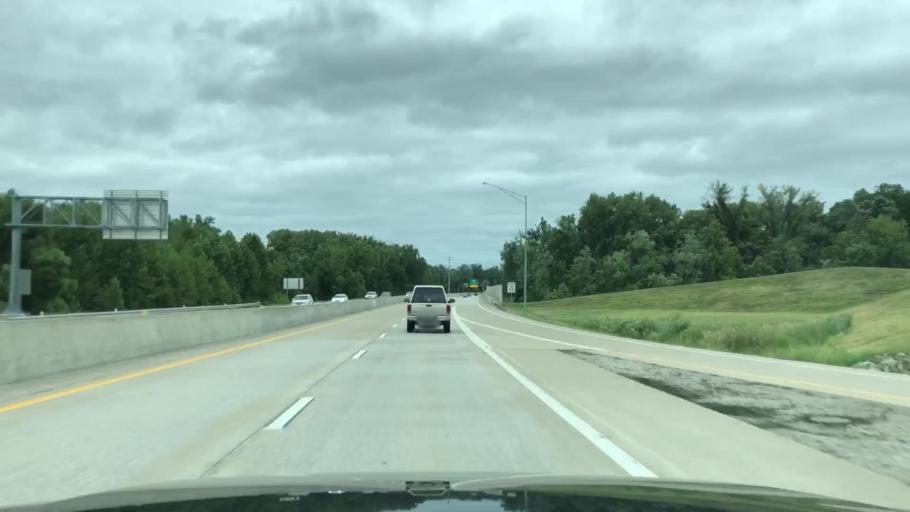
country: US
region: Missouri
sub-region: Saint Louis County
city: Town and Country
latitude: 38.6782
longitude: -90.4934
